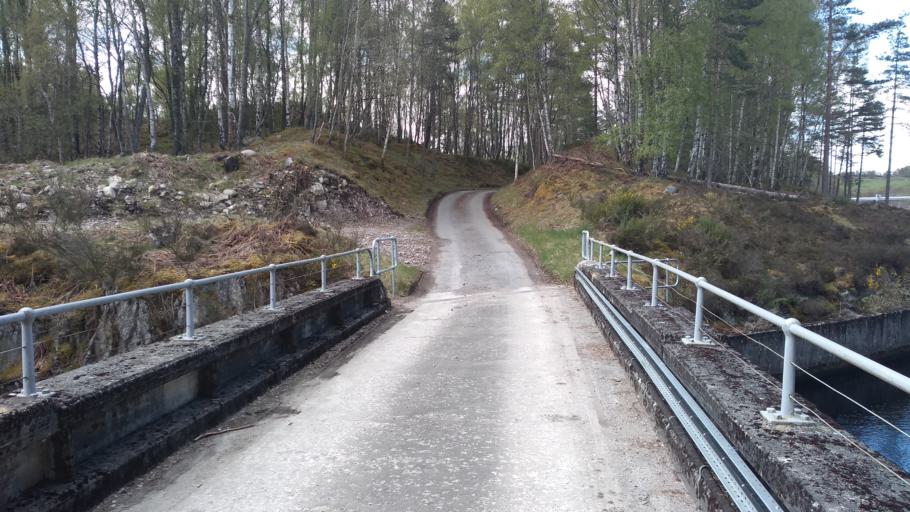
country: GB
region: Scotland
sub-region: Perth and Kinross
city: Aberfeldy
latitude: 56.7060
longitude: -4.0837
